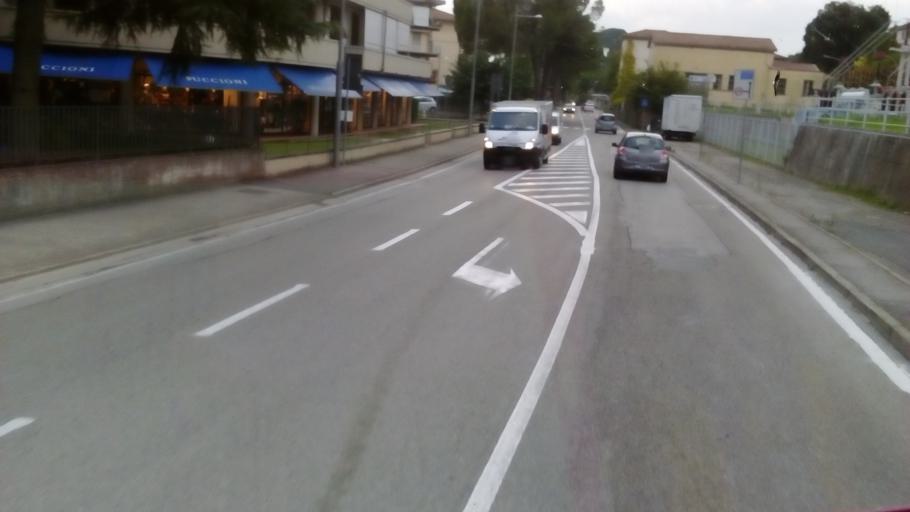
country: IT
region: Tuscany
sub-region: Province of Florence
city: Castelfiorentino
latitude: 43.6126
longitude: 10.9684
